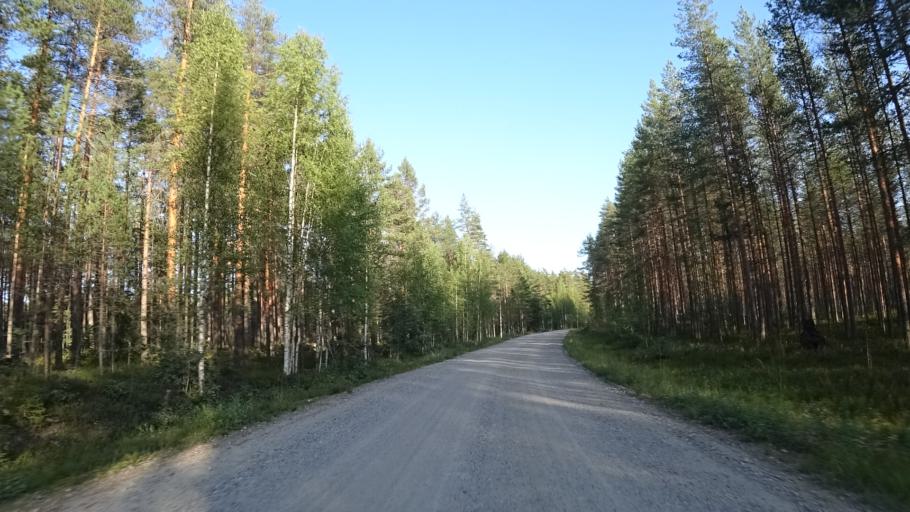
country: FI
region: North Karelia
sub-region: Joensuu
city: Ilomantsi
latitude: 63.1370
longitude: 30.7034
